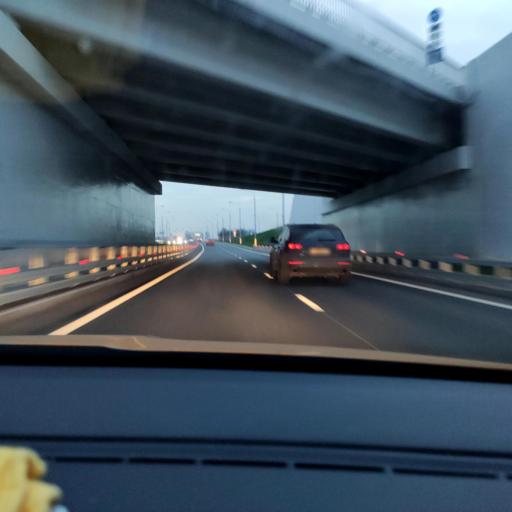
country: RU
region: Moscow
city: Vorob'yovo
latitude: 55.7312
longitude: 37.5228
